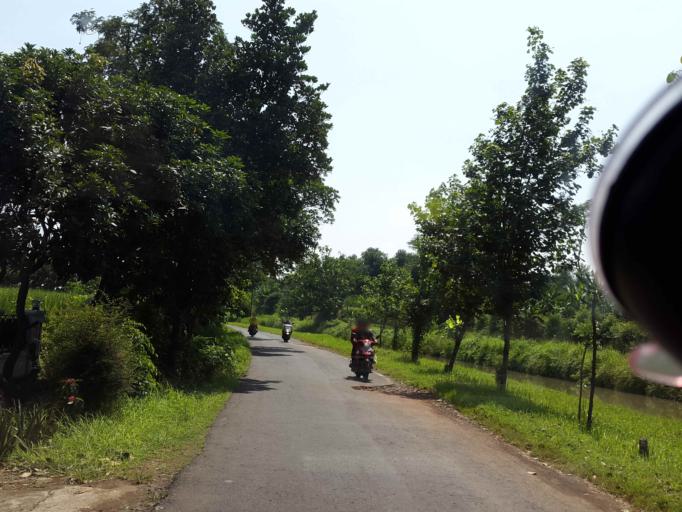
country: ID
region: Central Java
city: Pemalang
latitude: -6.9471
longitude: 109.3826
